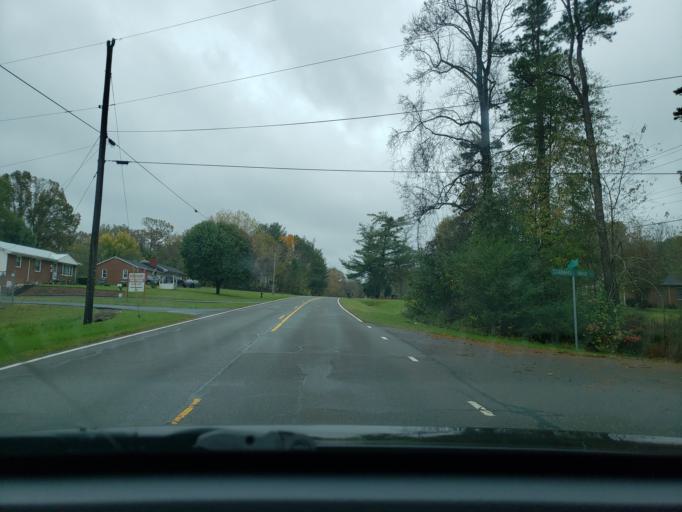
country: US
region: North Carolina
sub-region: Stokes County
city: Walnut Cove
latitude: 36.2767
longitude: -80.1446
